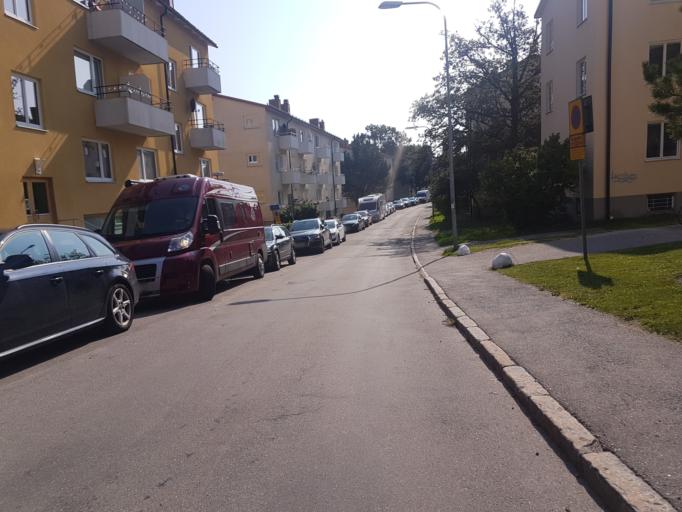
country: SE
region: Stockholm
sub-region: Stockholms Kommun
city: OEstermalm
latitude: 59.2972
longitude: 18.1035
